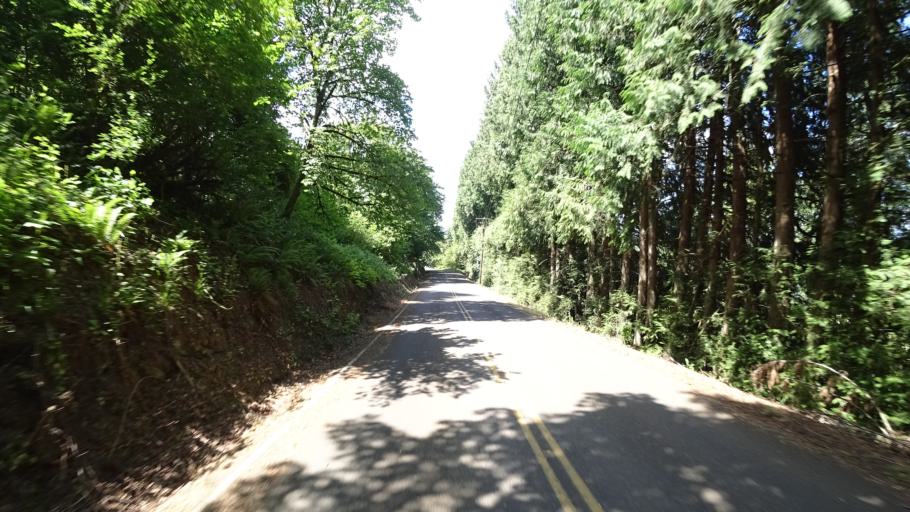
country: US
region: Oregon
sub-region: Washington County
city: Oak Hills
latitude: 45.6179
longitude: -122.8090
